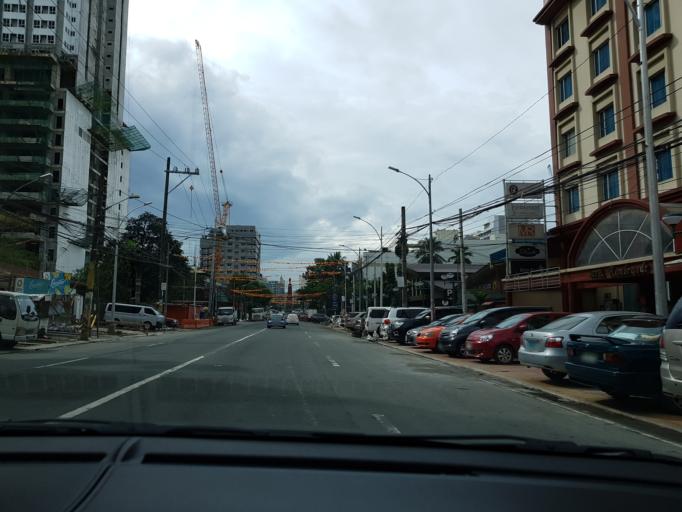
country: PH
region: Metro Manila
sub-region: Quezon City
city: Quezon City
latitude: 14.6377
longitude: 121.0360
